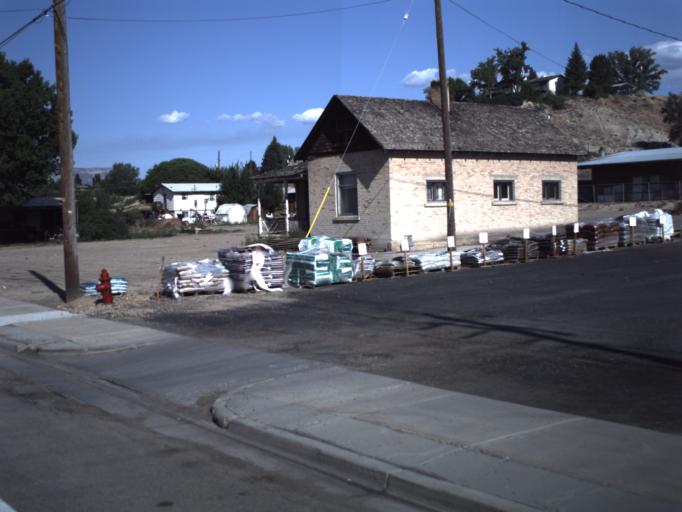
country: US
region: Utah
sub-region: Emery County
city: Castle Dale
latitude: 39.2119
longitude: -111.0106
